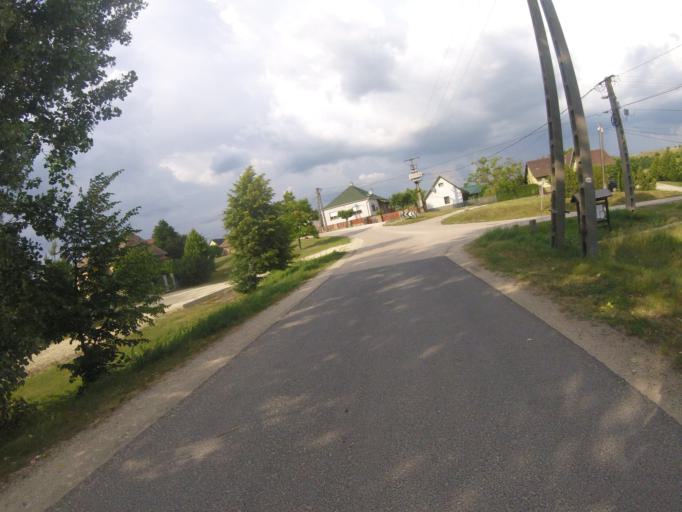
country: HU
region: Fejer
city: Szarliget
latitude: 47.4795
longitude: 18.5210
